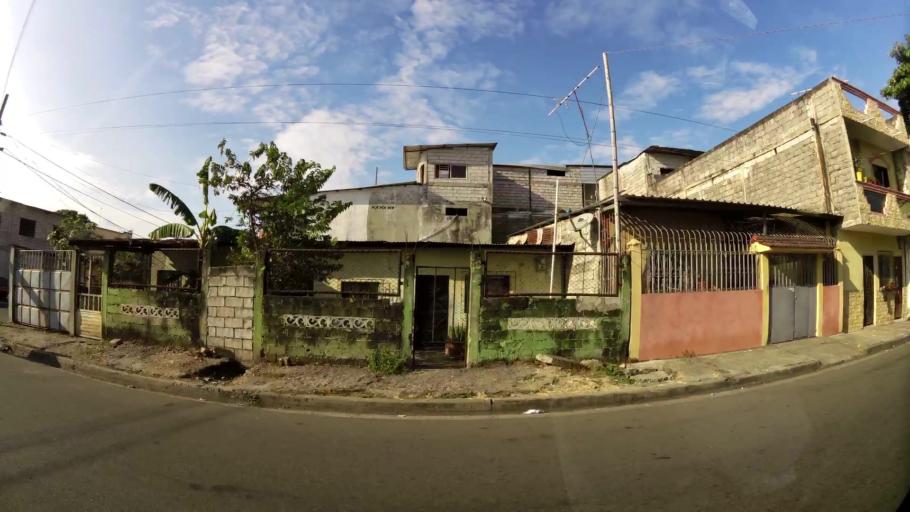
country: EC
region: Guayas
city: Guayaquil
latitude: -2.2149
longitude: -79.9224
